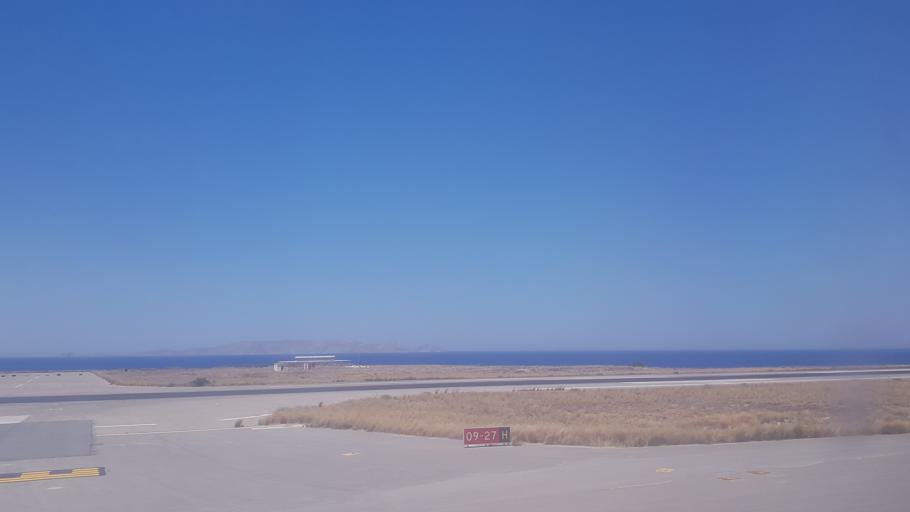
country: GR
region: Crete
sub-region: Nomos Irakleiou
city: Nea Alikarnassos
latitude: 35.3385
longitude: 25.1841
